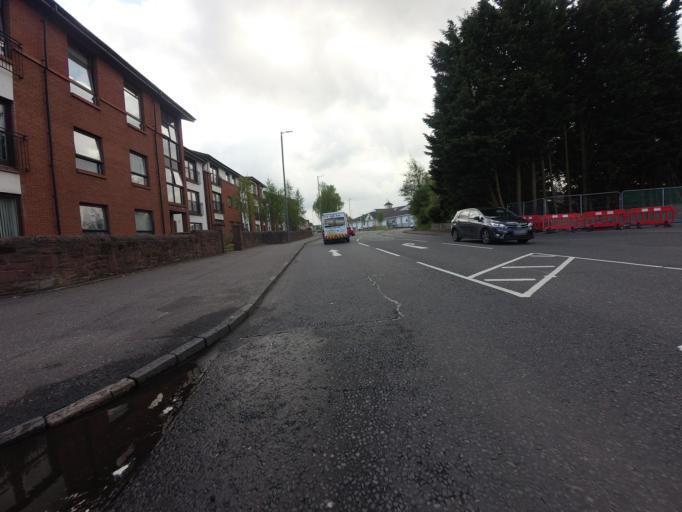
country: GB
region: Scotland
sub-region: Falkirk
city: Falkirk
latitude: 56.0184
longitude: -3.7925
